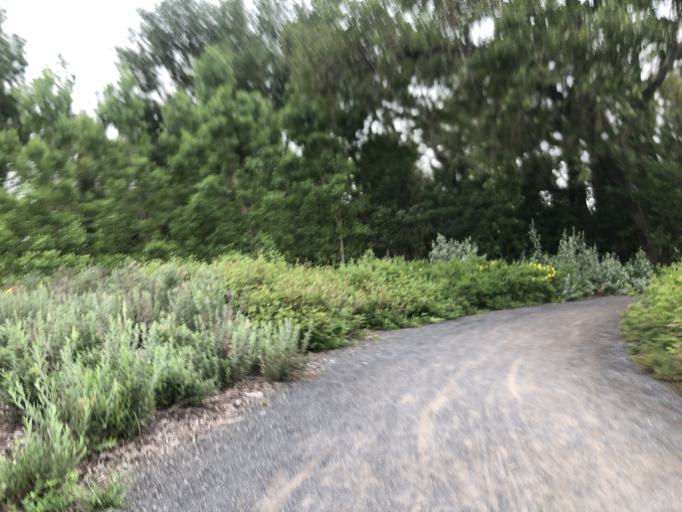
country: CA
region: Alberta
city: Calgary
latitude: 51.0430
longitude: -114.0143
